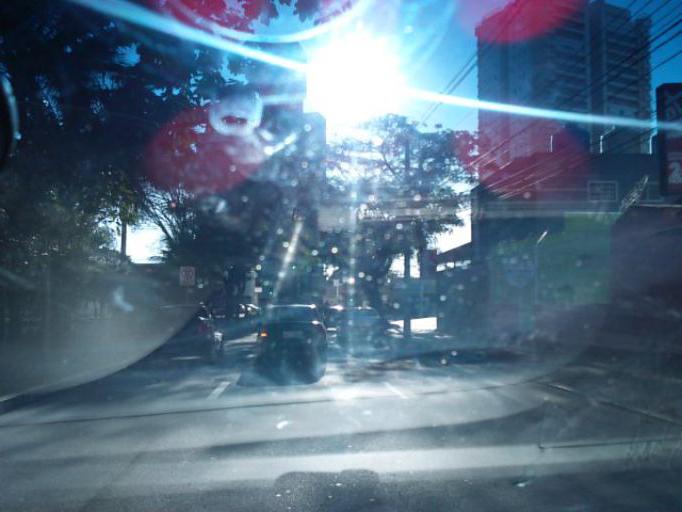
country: BR
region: Sao Paulo
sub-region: Sao Jose Dos Campos
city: Sao Jose dos Campos
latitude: -23.1969
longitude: -45.8974
